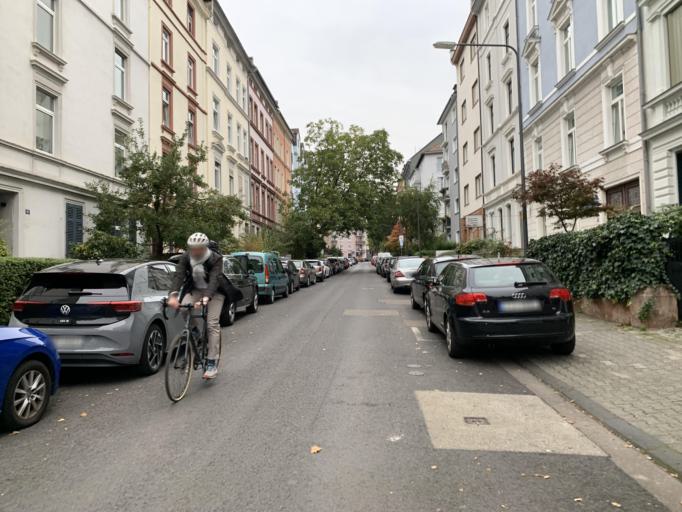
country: DE
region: Hesse
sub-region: Regierungsbezirk Darmstadt
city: Frankfurt am Main
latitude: 50.1212
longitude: 8.6947
